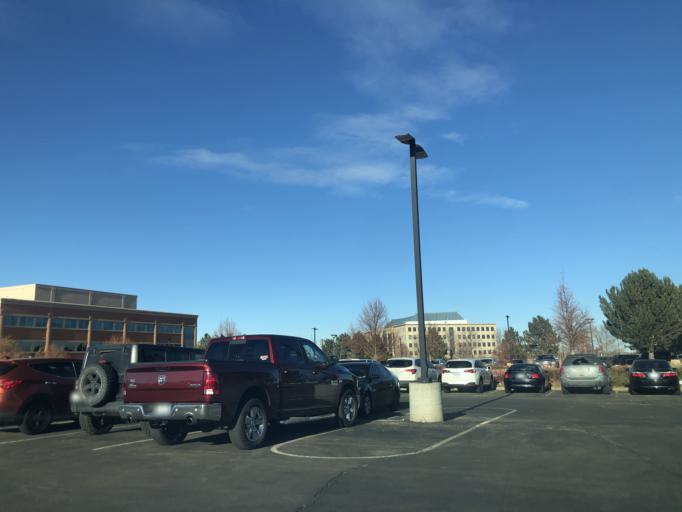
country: US
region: Colorado
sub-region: Adams County
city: Aurora
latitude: 39.7073
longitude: -104.8140
